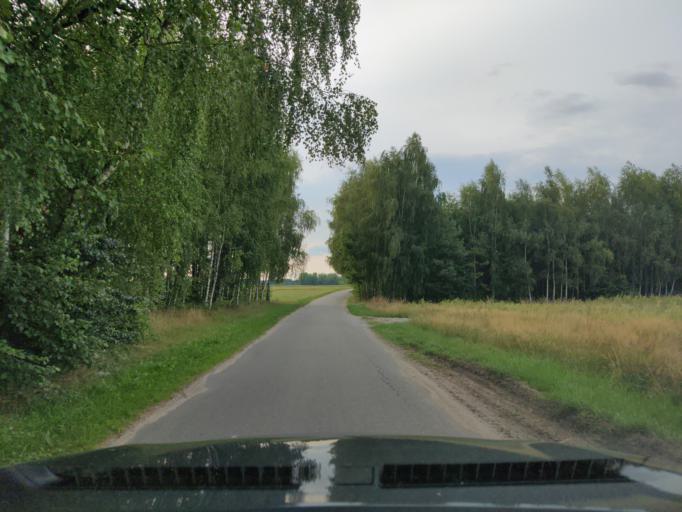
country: PL
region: Masovian Voivodeship
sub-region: Powiat pultuski
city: Obryte
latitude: 52.7435
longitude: 21.2447
